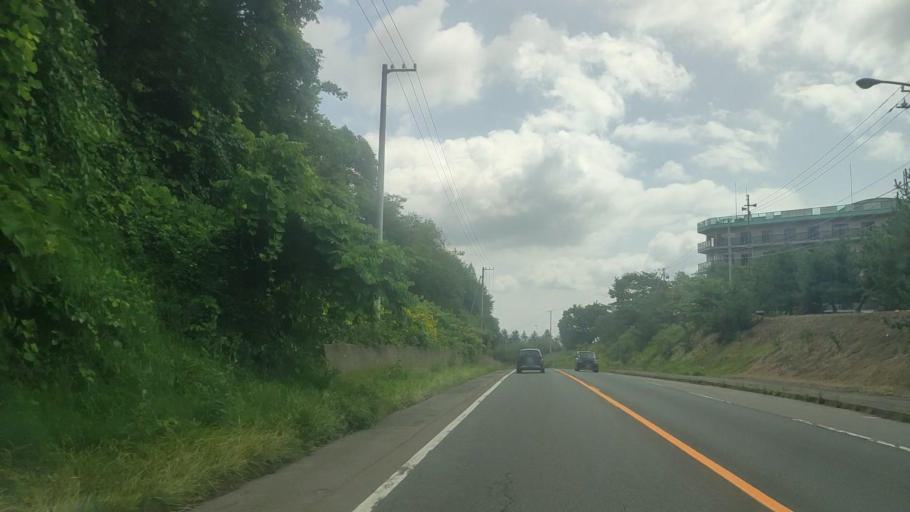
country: JP
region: Hokkaido
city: Date
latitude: 42.5600
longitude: 140.7461
